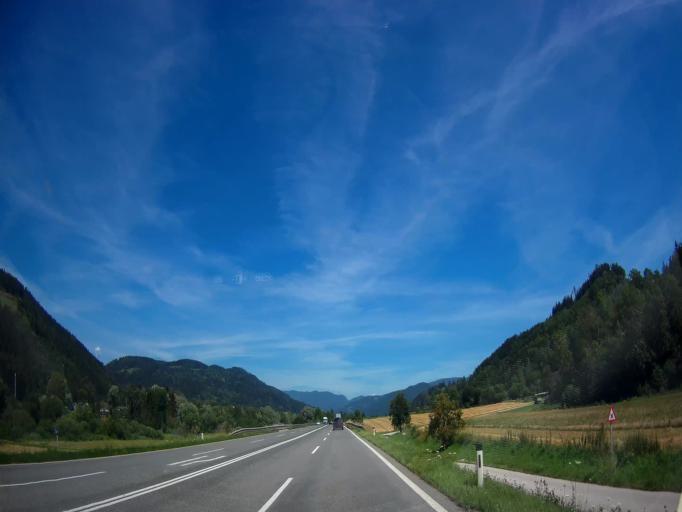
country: AT
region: Carinthia
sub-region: Politischer Bezirk Sankt Veit an der Glan
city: Micheldorf
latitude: 46.9049
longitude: 14.4389
